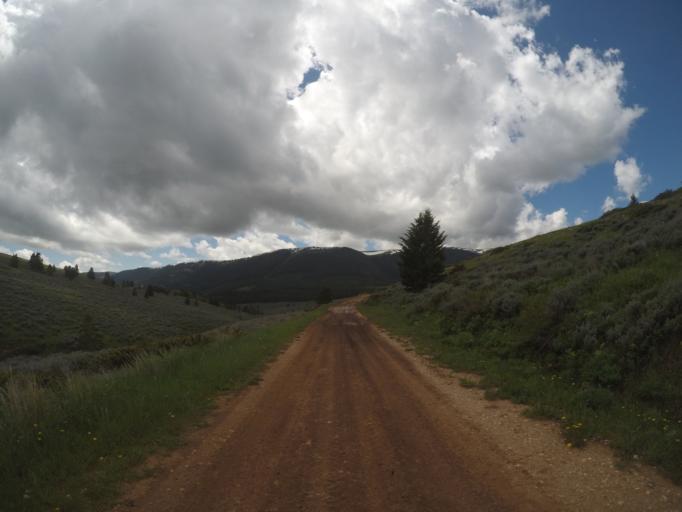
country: US
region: Wyoming
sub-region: Big Horn County
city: Lovell
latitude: 45.1811
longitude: -108.4375
